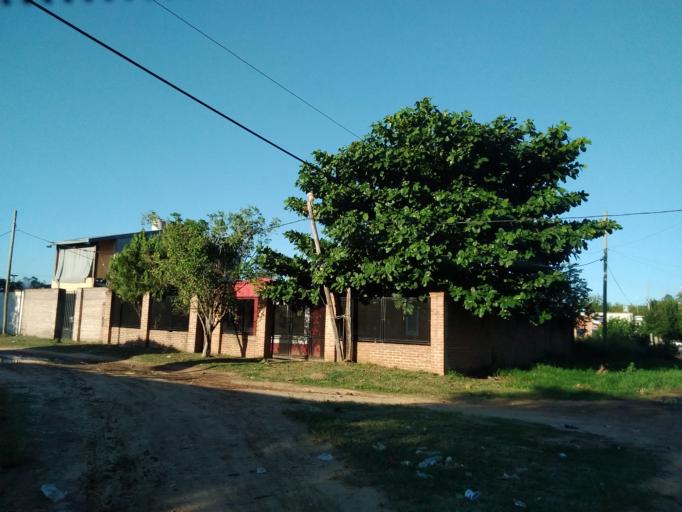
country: AR
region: Corrientes
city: Corrientes
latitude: -27.5069
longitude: -58.8032
